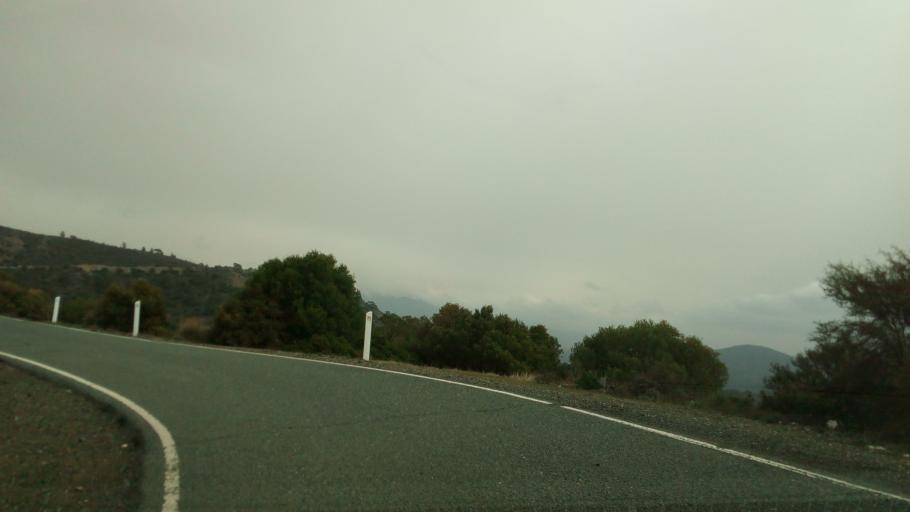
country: CY
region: Limassol
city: Mouttagiaka
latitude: 34.8086
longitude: 33.0923
